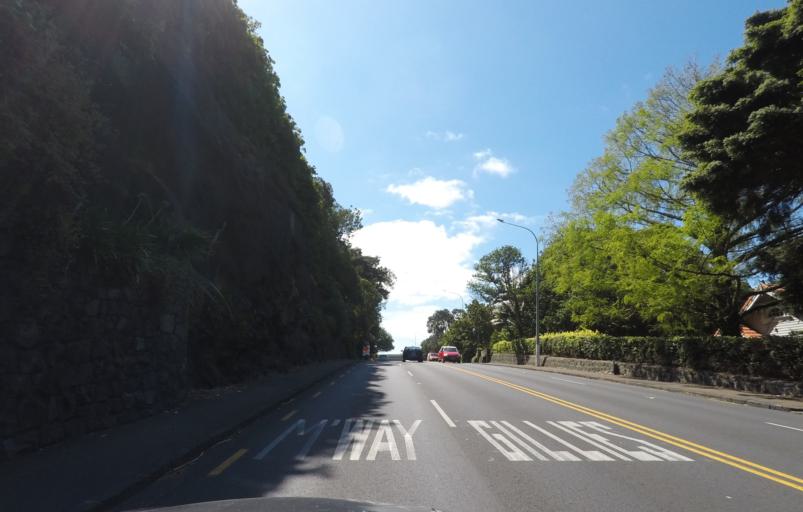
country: NZ
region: Auckland
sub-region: Auckland
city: Auckland
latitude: -36.8742
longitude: 174.7737
